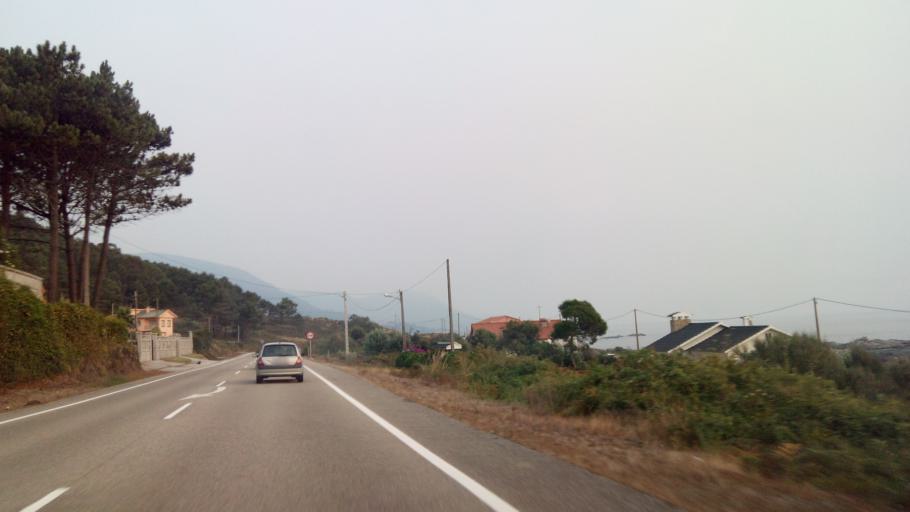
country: ES
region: Galicia
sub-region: Provincia de Pontevedra
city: Oia
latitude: 42.0625
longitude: -8.8902
